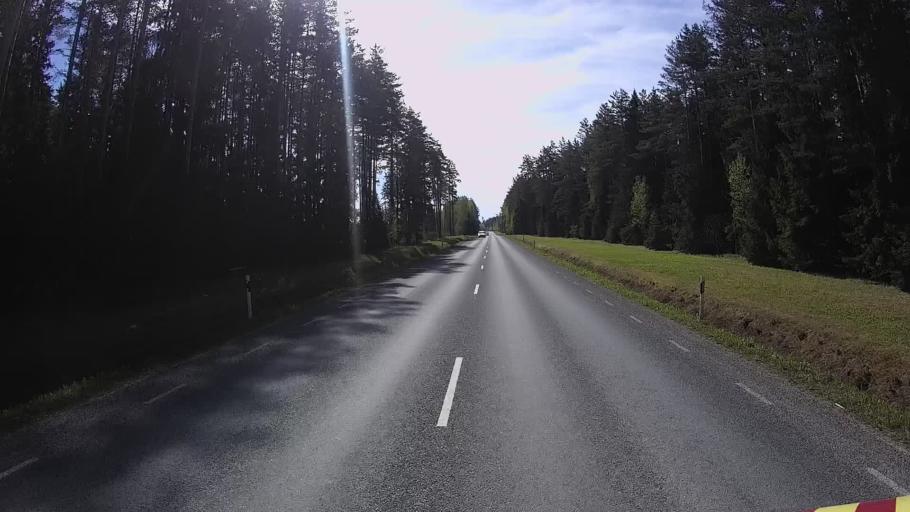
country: EE
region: Polvamaa
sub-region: Polva linn
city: Polva
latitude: 58.1710
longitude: 27.1365
